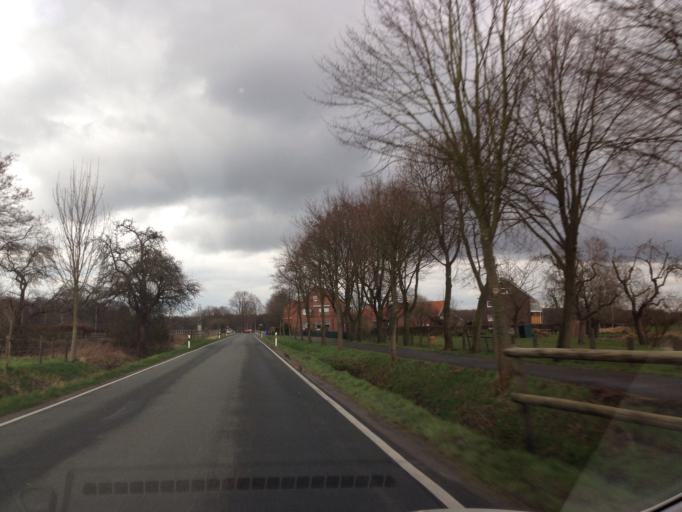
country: DE
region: North Rhine-Westphalia
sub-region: Regierungsbezirk Munster
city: Senden
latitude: 51.8302
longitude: 7.5398
